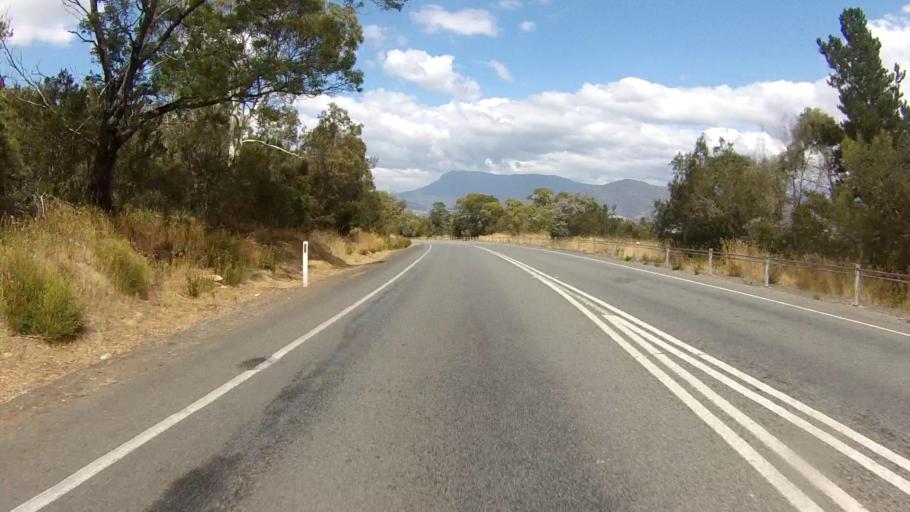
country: AU
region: Tasmania
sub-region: Brighton
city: Old Beach
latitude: -42.7717
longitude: 147.2688
